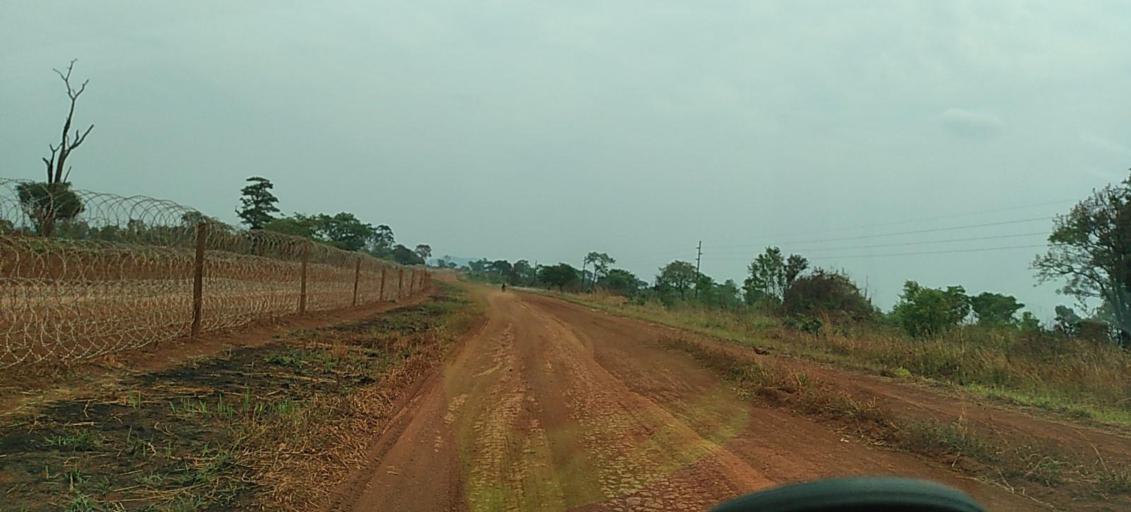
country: ZM
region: North-Western
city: Kansanshi
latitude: -12.0861
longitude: 26.4834
